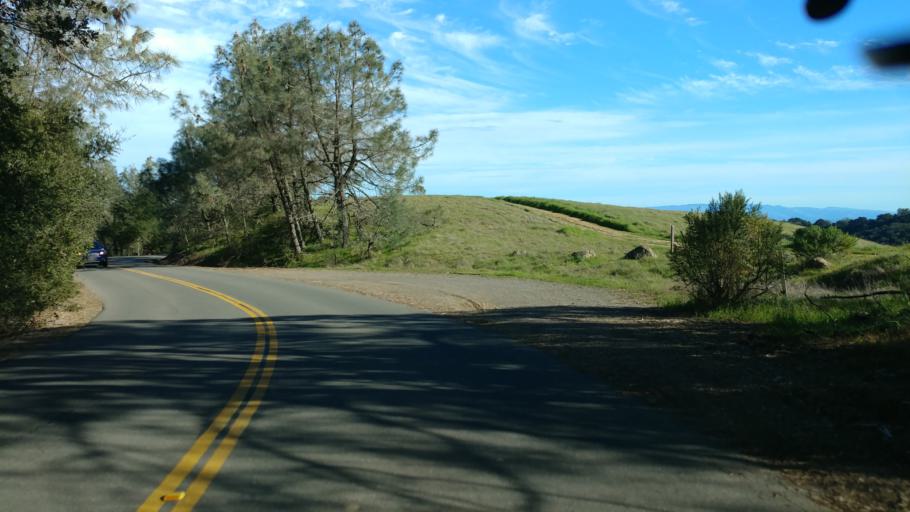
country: US
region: California
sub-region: Contra Costa County
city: Diablo
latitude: 37.8535
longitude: -121.9306
